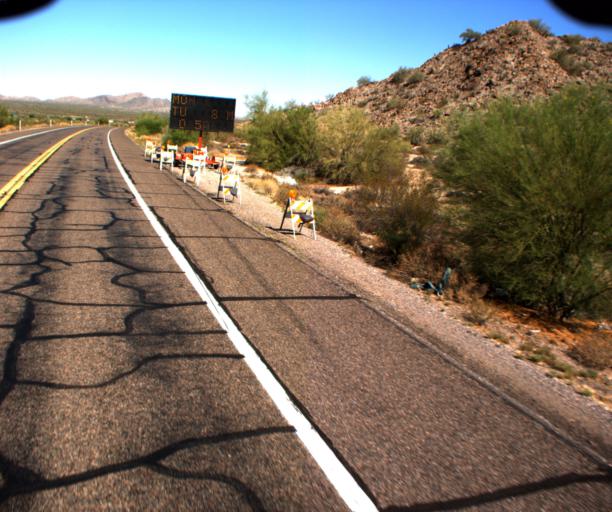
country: US
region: Arizona
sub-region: Pinal County
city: Sacaton
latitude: 33.0037
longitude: -111.7451
